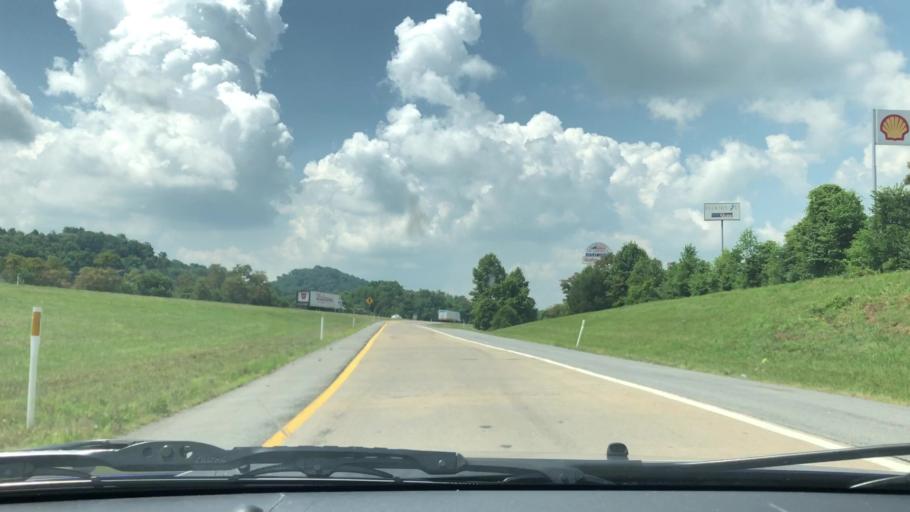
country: US
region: Tennessee
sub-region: Sullivan County
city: Blountville
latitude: 36.5336
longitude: -82.3890
